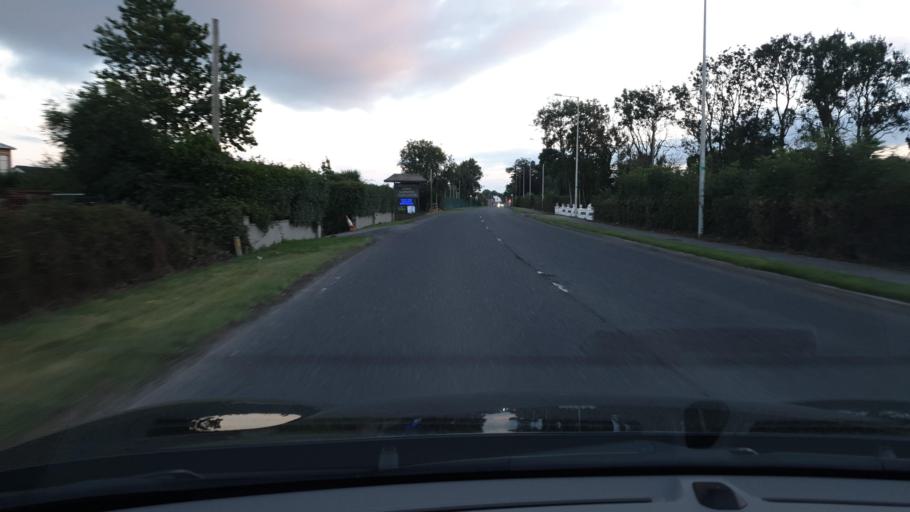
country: IE
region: Leinster
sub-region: An Mhi
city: Duleek
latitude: 53.6710
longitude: -6.3952
